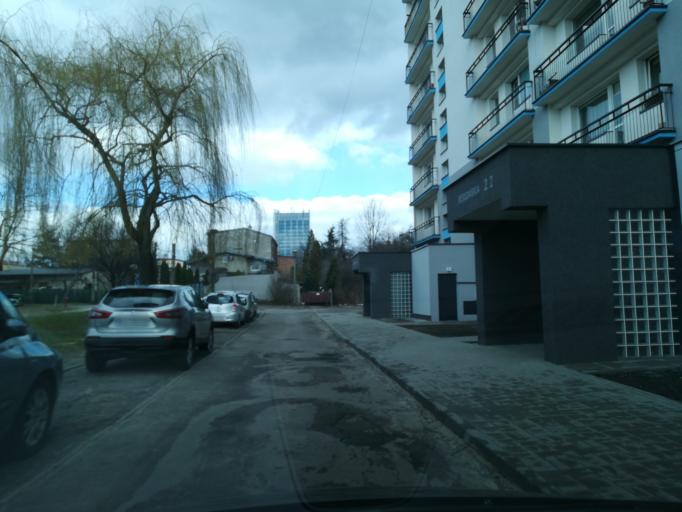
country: PL
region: Silesian Voivodeship
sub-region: Sosnowiec
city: Sosnowiec
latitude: 50.2942
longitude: 19.1324
